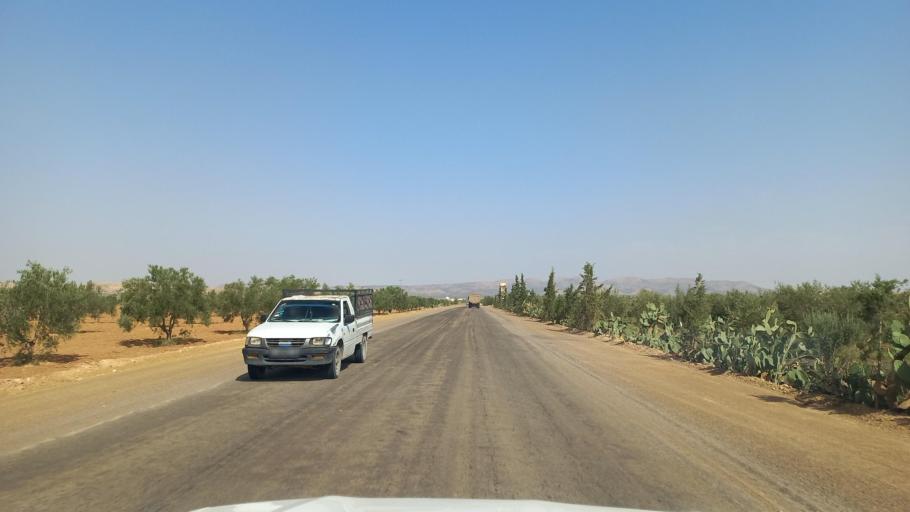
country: TN
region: Al Qasrayn
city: Sbiba
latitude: 35.3497
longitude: 9.0523
